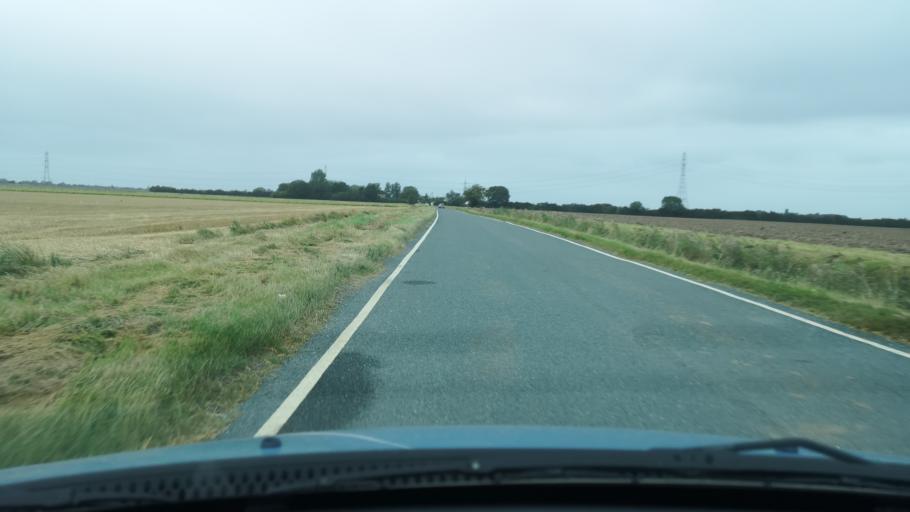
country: GB
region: England
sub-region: North Lincolnshire
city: Burton upon Stather
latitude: 53.6974
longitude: -0.7292
